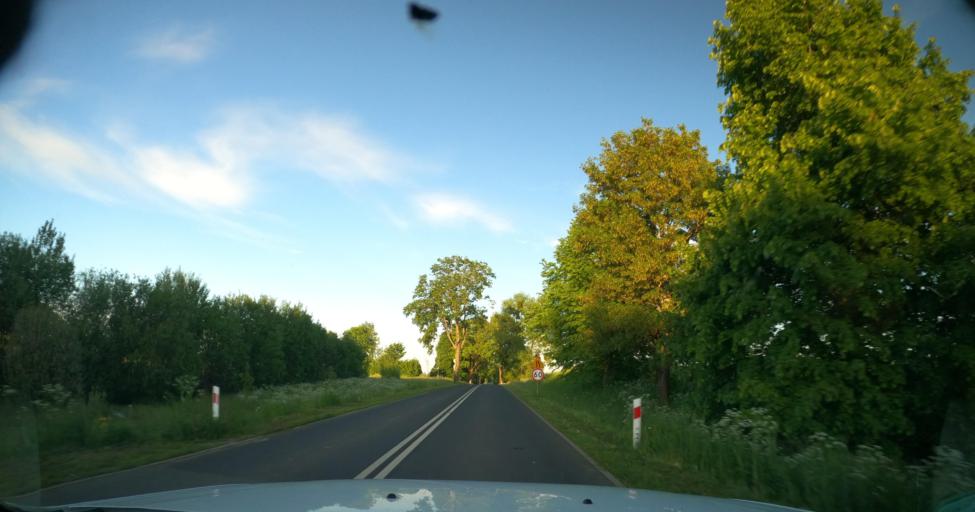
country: PL
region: Warmian-Masurian Voivodeship
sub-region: Powiat lidzbarski
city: Lidzbark Warminski
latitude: 54.1455
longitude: 20.4843
